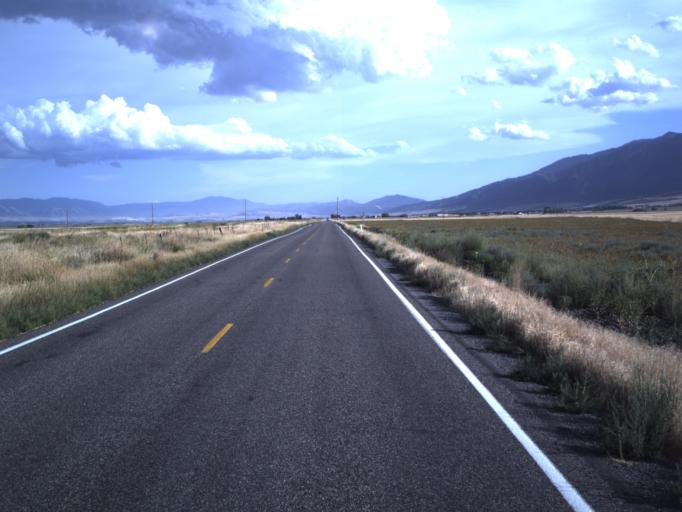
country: US
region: Utah
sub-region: Cache County
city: Benson
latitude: 41.7924
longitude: -111.9893
